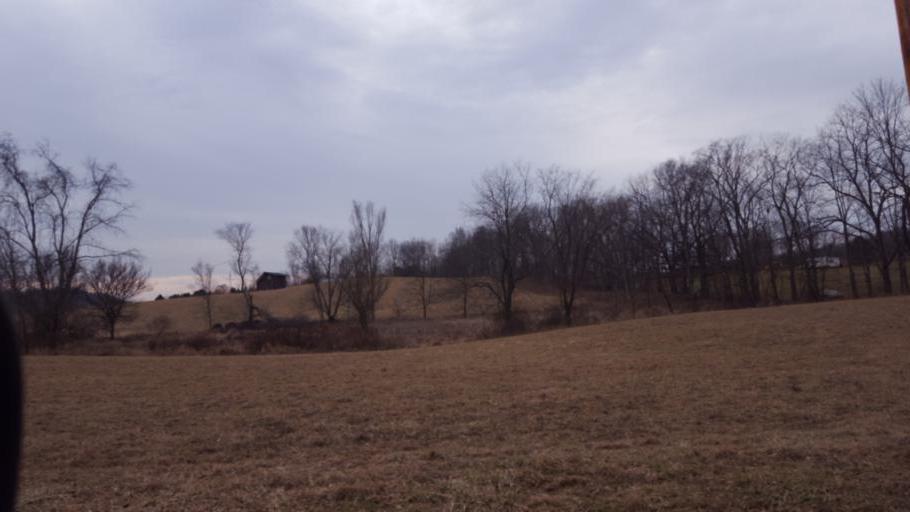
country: US
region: Ohio
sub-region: Ashland County
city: Loudonville
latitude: 40.7045
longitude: -82.2882
